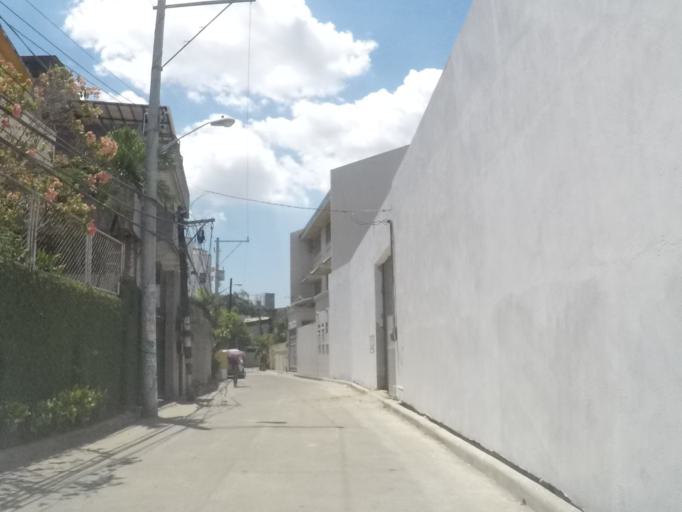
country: PH
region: Metro Manila
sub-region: San Juan
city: San Juan
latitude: 14.6002
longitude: 121.0270
